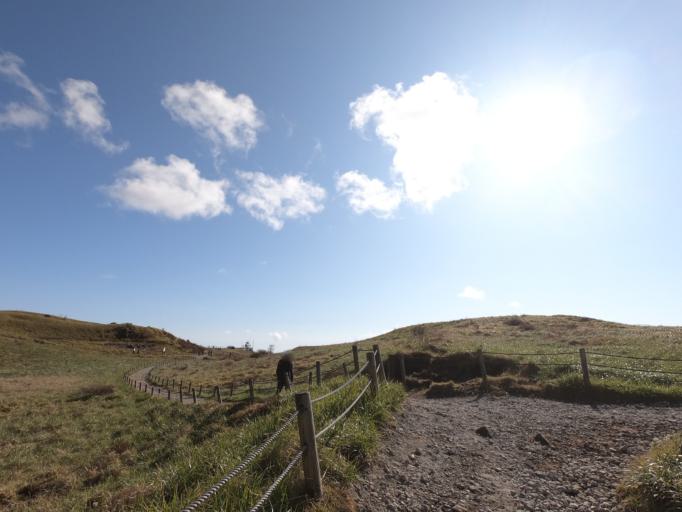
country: JP
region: Kanagawa
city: Hakone
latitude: 35.2237
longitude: 139.0248
